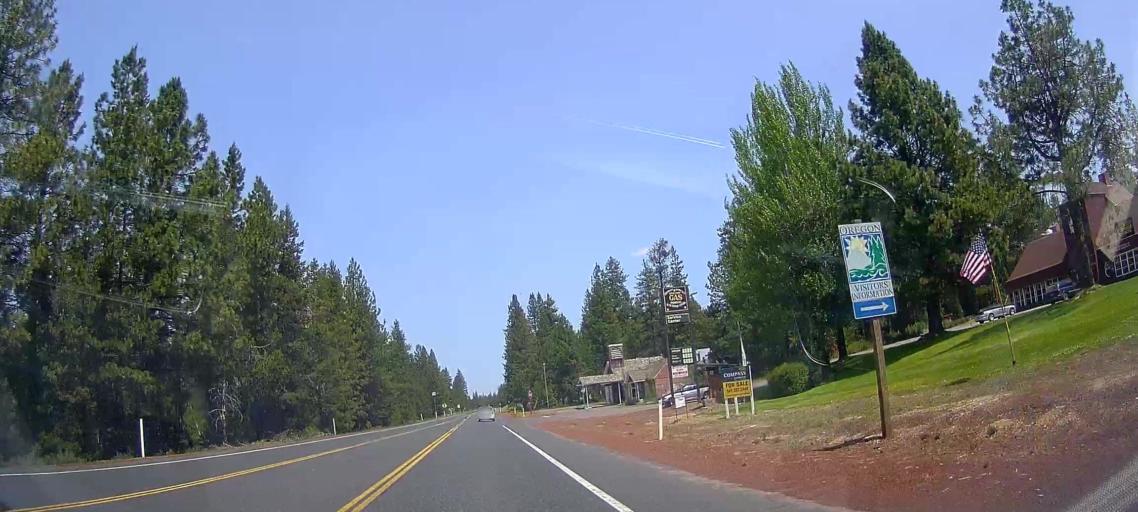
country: US
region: Oregon
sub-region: Deschutes County
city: La Pine
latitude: 43.4784
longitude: -121.6875
